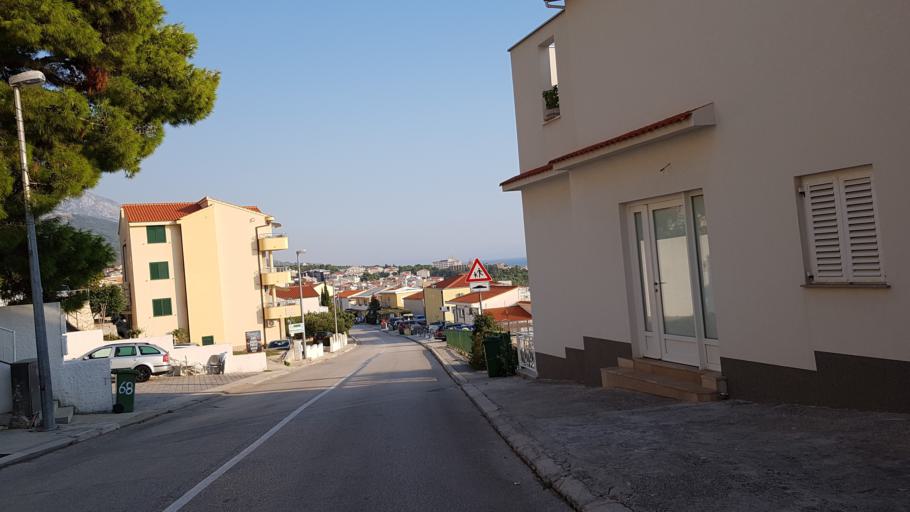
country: HR
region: Splitsko-Dalmatinska
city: Baska Voda
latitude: 43.3618
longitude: 16.9454
